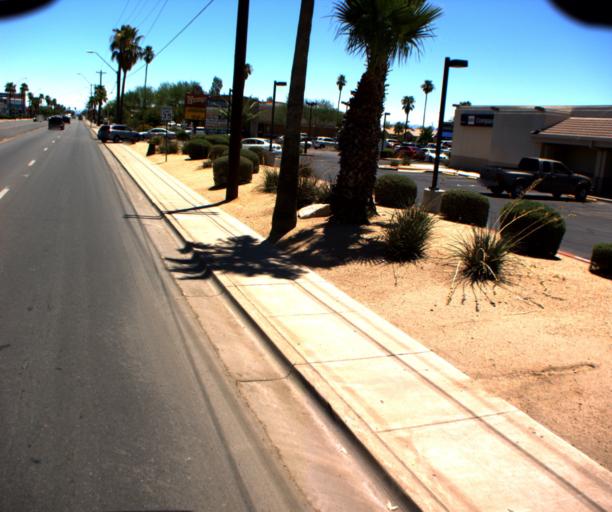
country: US
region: Arizona
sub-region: Pinal County
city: Casa Grande
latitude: 32.8795
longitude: -111.7398
